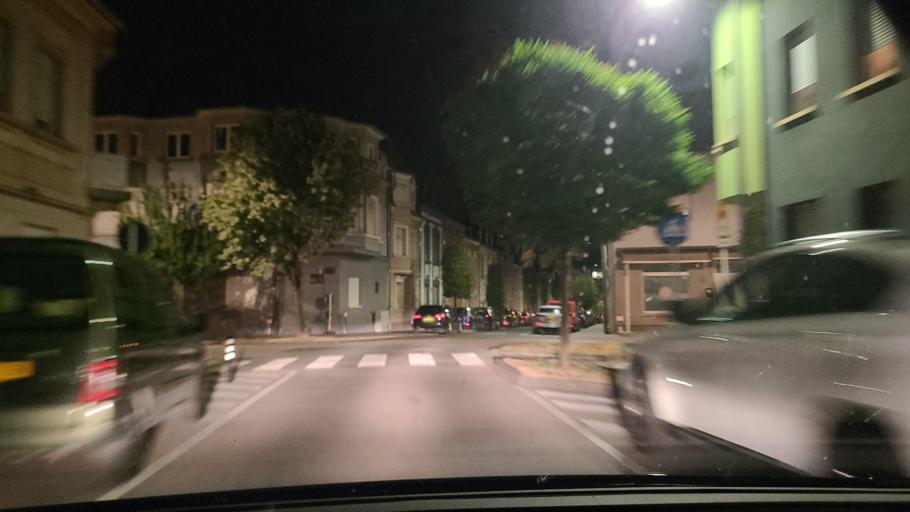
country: LU
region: Luxembourg
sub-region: Canton d'Esch-sur-Alzette
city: Obercorn
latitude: 49.5198
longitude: 5.8977
